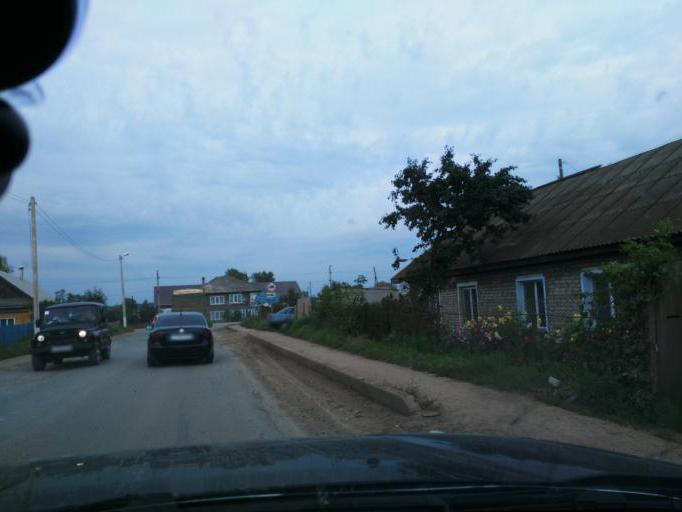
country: RU
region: Perm
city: Kuyeda
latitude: 56.4264
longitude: 55.5809
